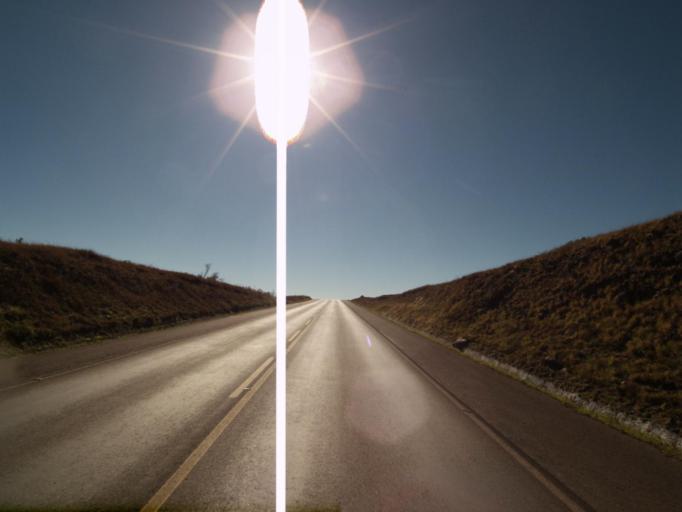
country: BR
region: Parana
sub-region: Palmas
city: Palmas
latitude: -26.7670
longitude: -51.6714
